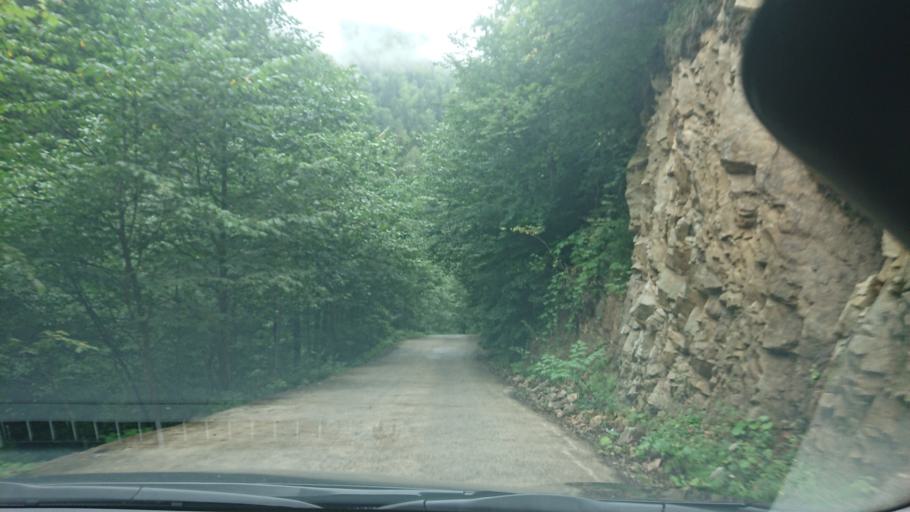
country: TR
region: Gumushane
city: Kurtun
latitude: 40.6680
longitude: 39.0392
